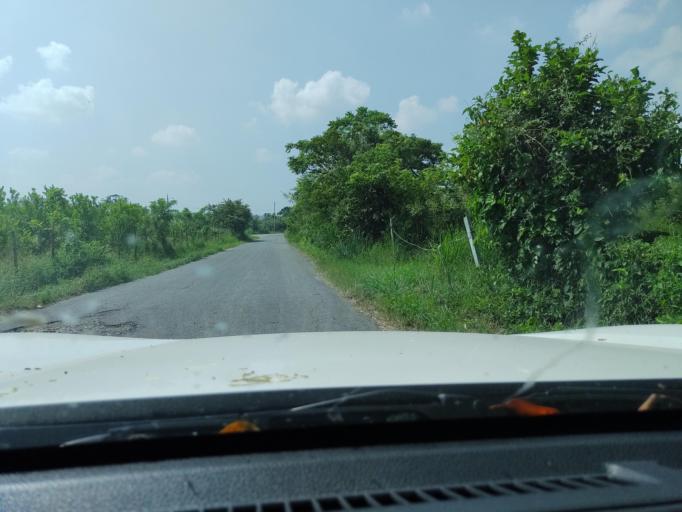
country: MX
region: Veracruz
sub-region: Martinez de la Torre
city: El Progreso
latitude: 20.0707
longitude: -97.0100
